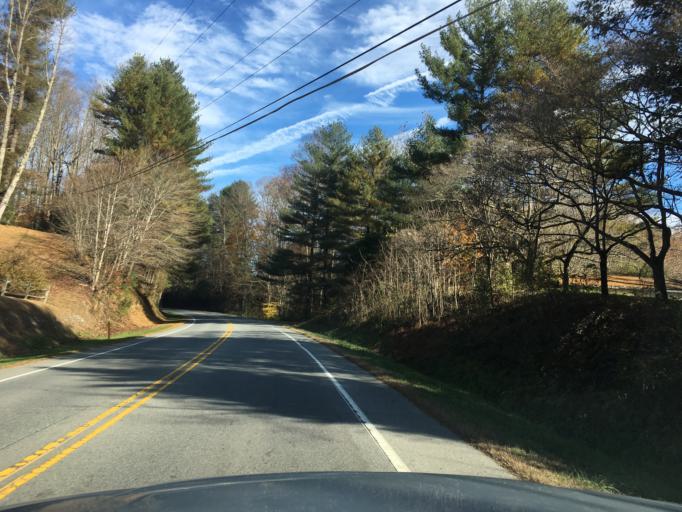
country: US
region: North Carolina
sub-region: Henderson County
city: Etowah
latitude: 35.2734
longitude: -82.6387
